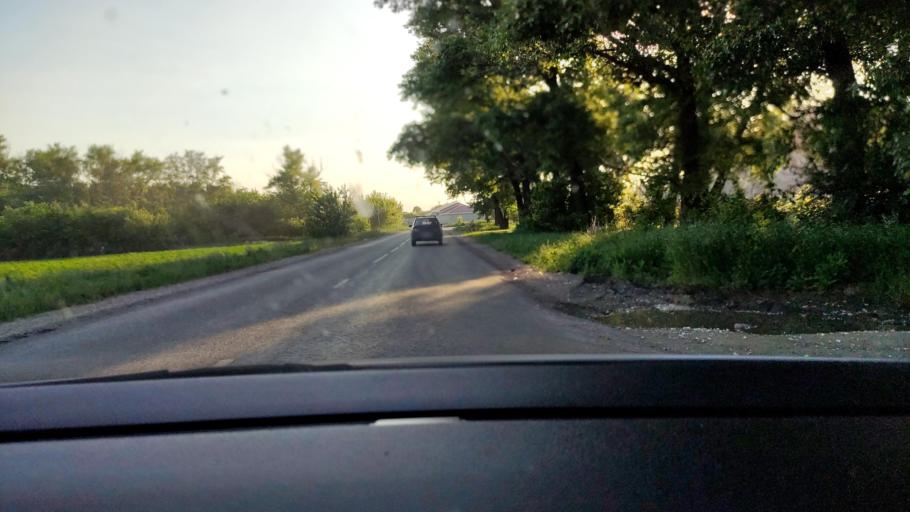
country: RU
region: Voronezj
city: Maslovka
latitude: 51.5354
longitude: 39.3440
